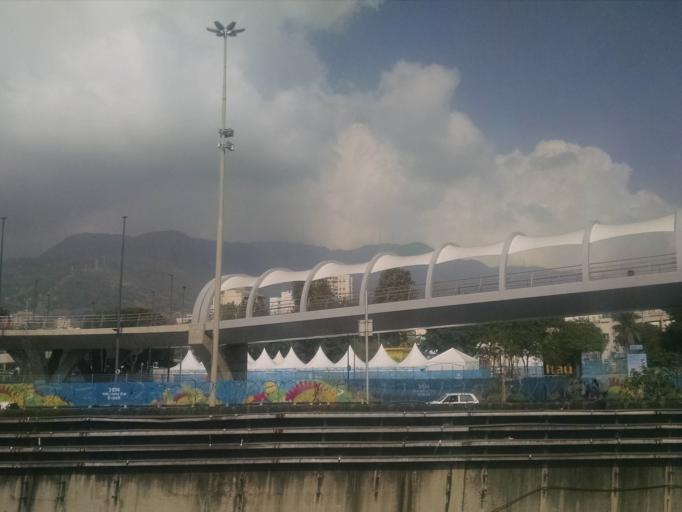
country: BR
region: Rio de Janeiro
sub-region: Rio De Janeiro
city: Rio de Janeiro
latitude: -22.9103
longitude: -43.2275
